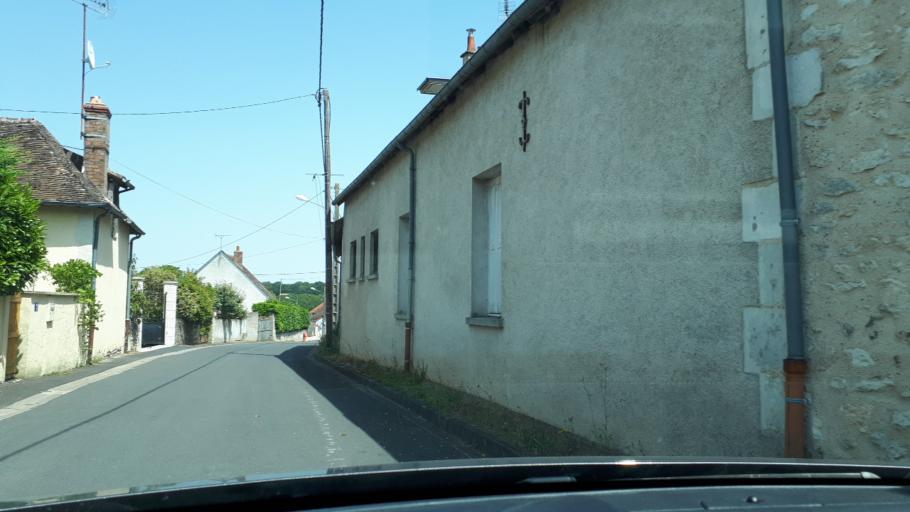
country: FR
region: Centre
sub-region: Departement du Loir-et-Cher
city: Vendome
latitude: 47.8172
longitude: 1.0592
